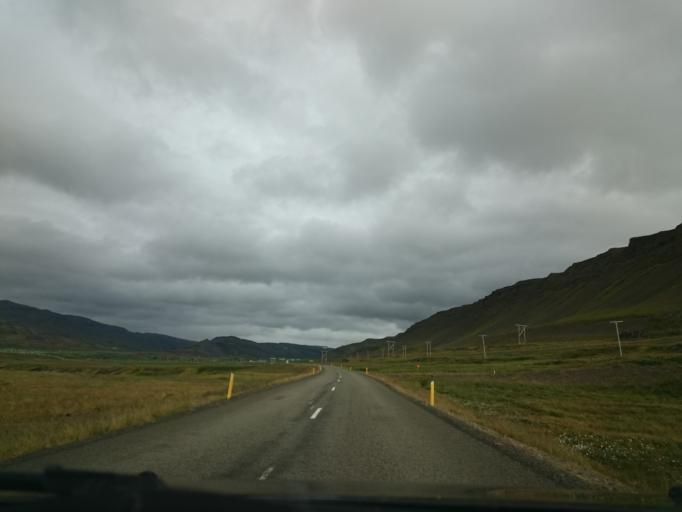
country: IS
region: West
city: Stykkisholmur
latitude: 65.4586
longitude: -21.9172
